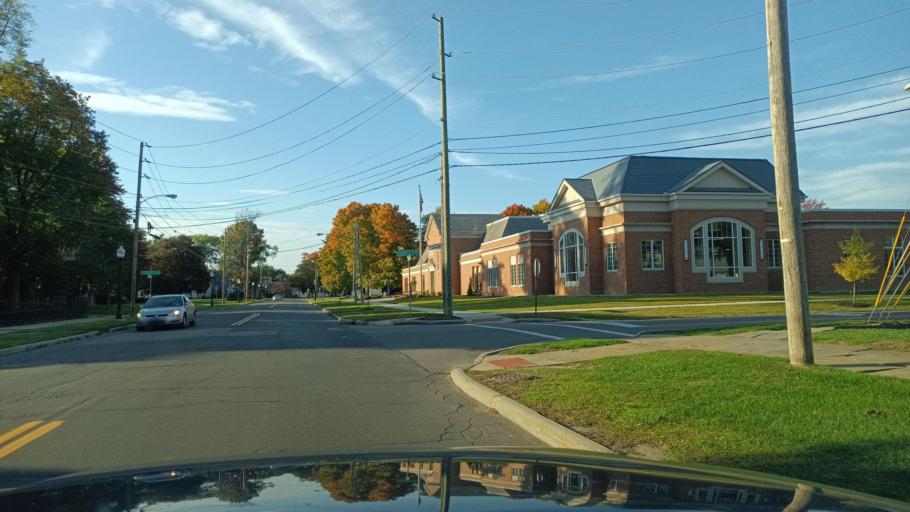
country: CN
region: Xinjiang Uygur Zizhiqu
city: Jiamu
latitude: 41.2394
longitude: 80.8224
